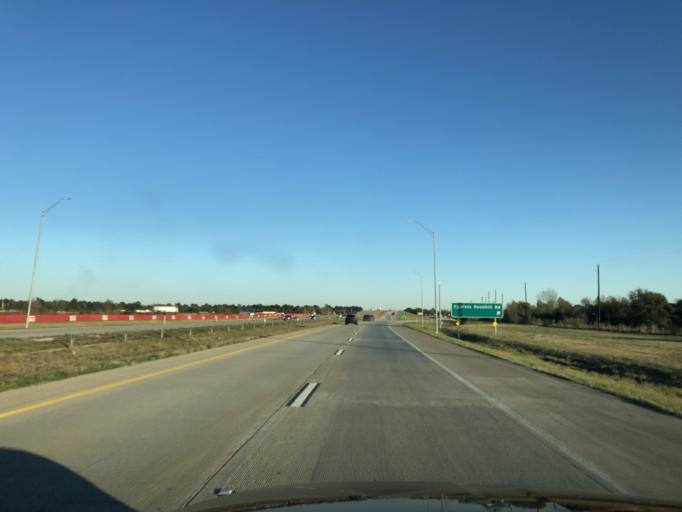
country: US
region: Texas
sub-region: Harris County
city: Cypress
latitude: 30.0539
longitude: -95.7049
